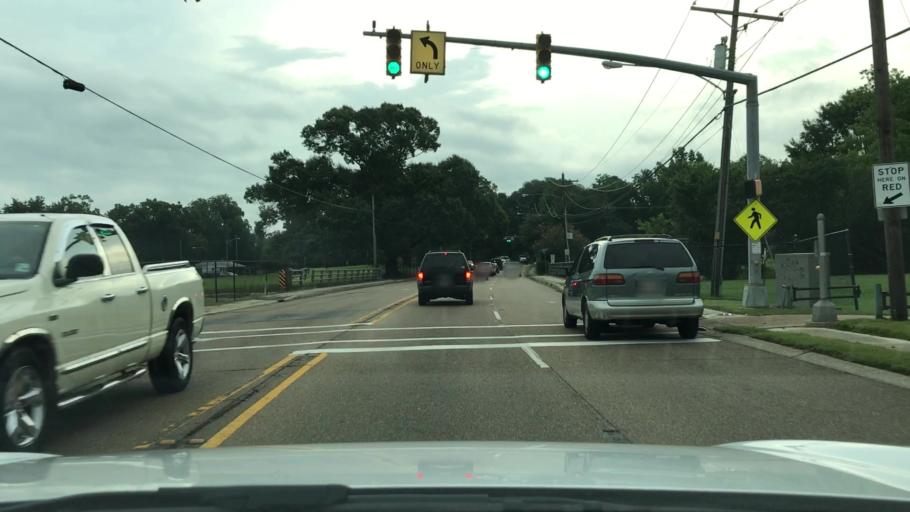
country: US
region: Louisiana
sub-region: East Baton Rouge Parish
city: Baton Rouge
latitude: 30.4356
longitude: -91.1335
